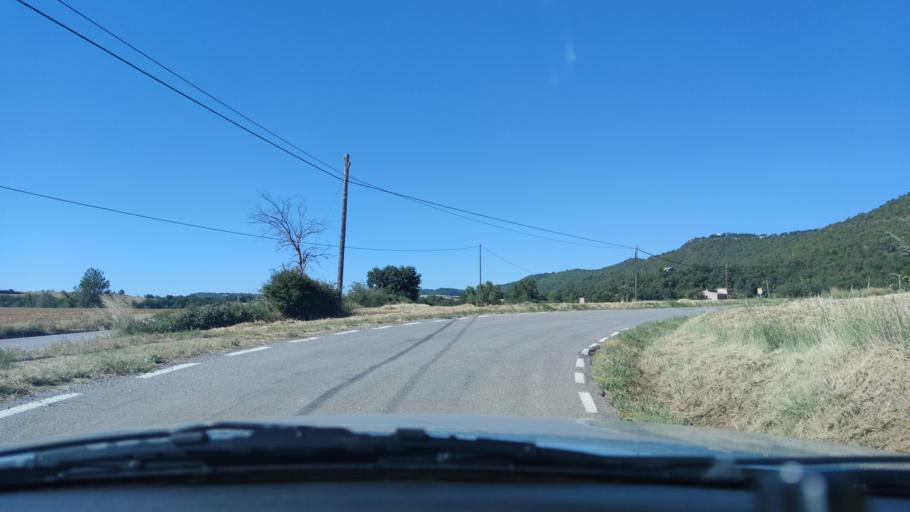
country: ES
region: Catalonia
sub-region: Provincia de Lleida
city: Solsona
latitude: 41.9771
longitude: 1.5034
